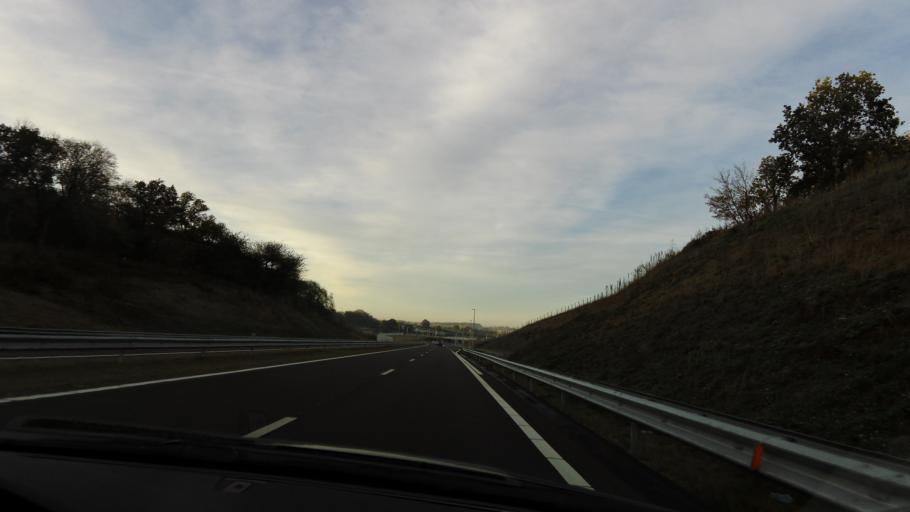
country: NL
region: Limburg
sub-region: Gemeente Heerlen
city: Hoensbroek
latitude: 50.9272
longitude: 5.9100
